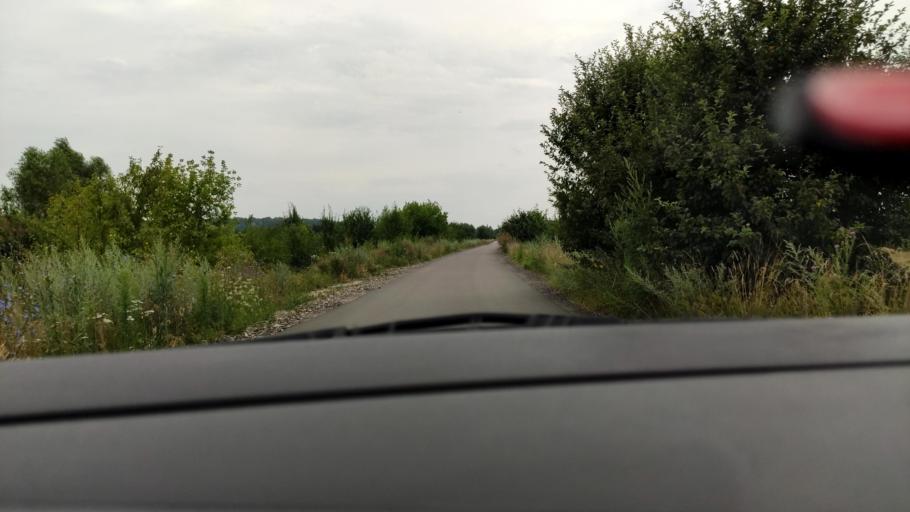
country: RU
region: Voronezj
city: Ramon'
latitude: 51.8995
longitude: 39.3500
